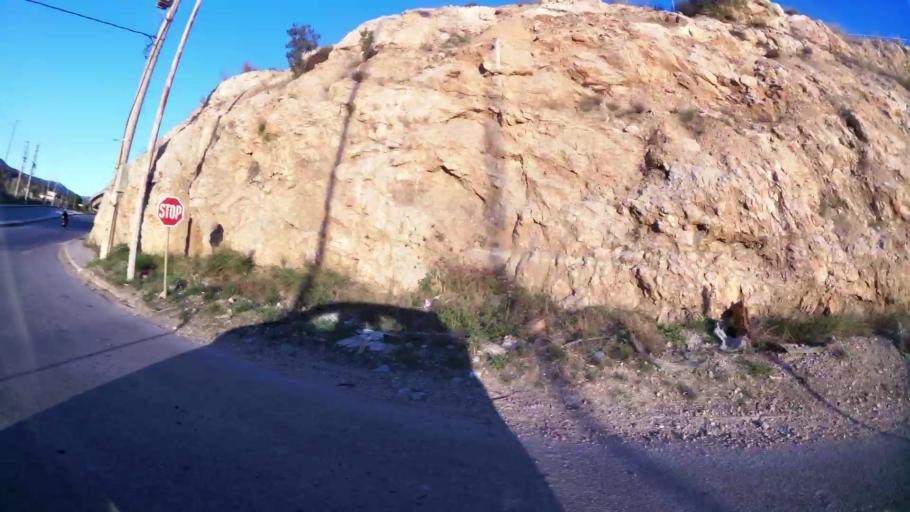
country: GR
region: Attica
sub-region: Nomarchia Athinas
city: Petroupolis
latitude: 38.0624
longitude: 23.6663
